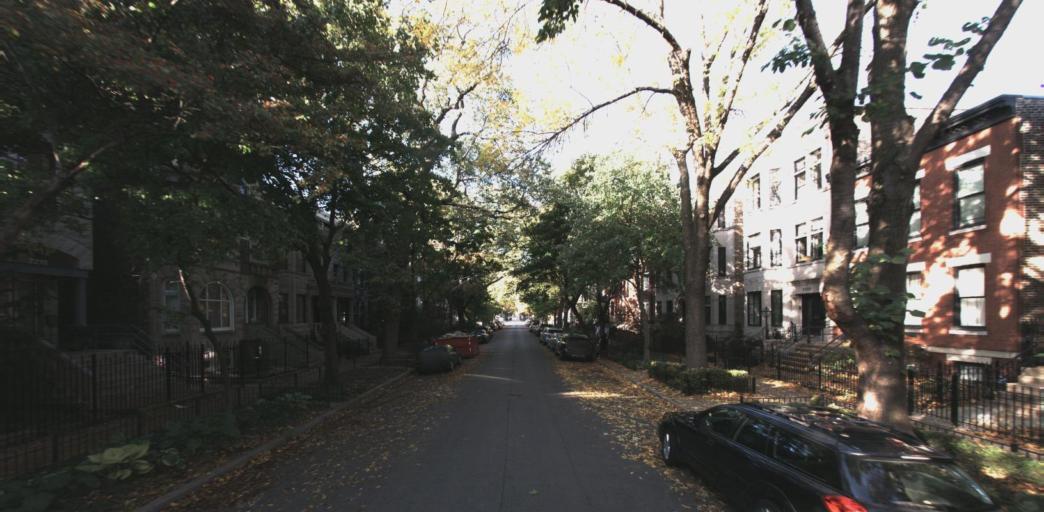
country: US
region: Illinois
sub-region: Cook County
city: Chicago
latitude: 41.9223
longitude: -87.6559
